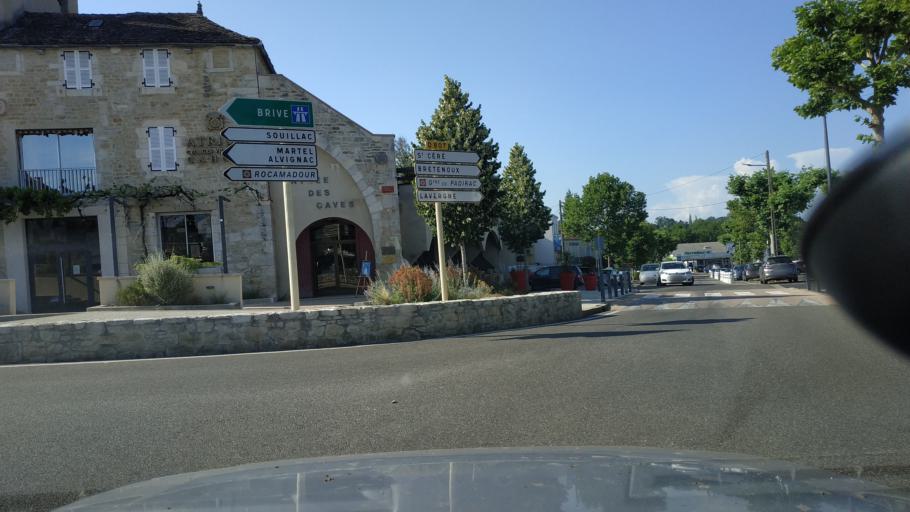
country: FR
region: Midi-Pyrenees
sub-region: Departement du Lot
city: Gramat
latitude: 44.7799
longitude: 1.7266
